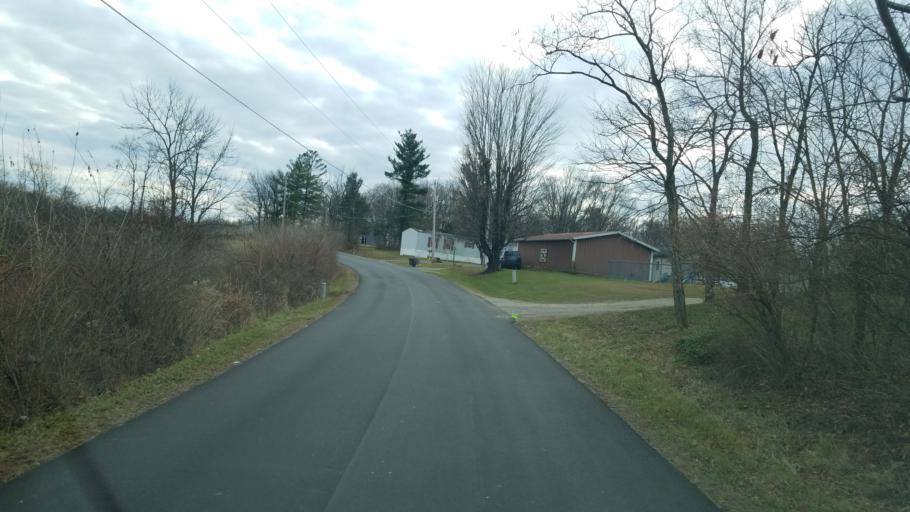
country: US
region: Ohio
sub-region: Highland County
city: Greenfield
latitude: 39.2034
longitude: -83.2688
